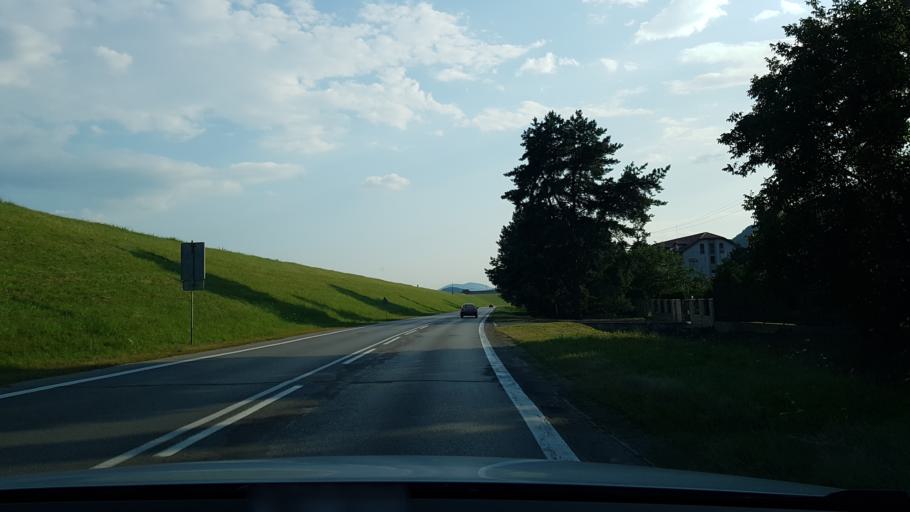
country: SK
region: Trenciansky
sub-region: Okres Povazska Bystrica
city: Povazska Bystrica
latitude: 49.1389
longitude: 18.4604
